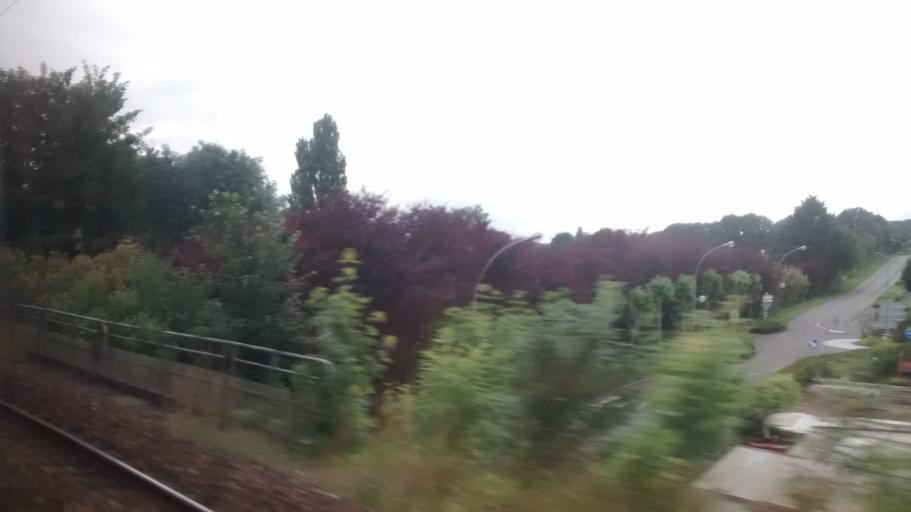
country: FR
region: Pays de la Loire
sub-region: Departement de la Mayenne
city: Montsurs
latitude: 48.1390
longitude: -0.5587
